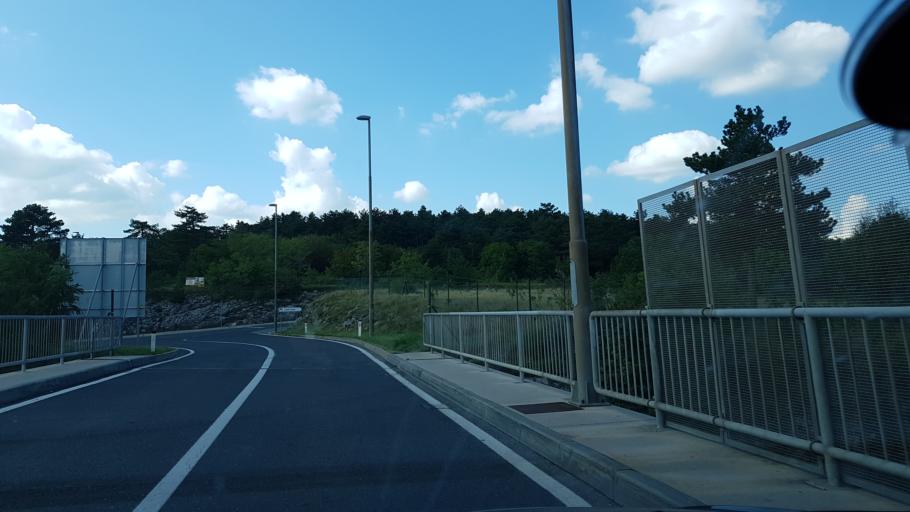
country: SI
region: Sezana
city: Sezana
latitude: 45.7029
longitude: 13.8424
